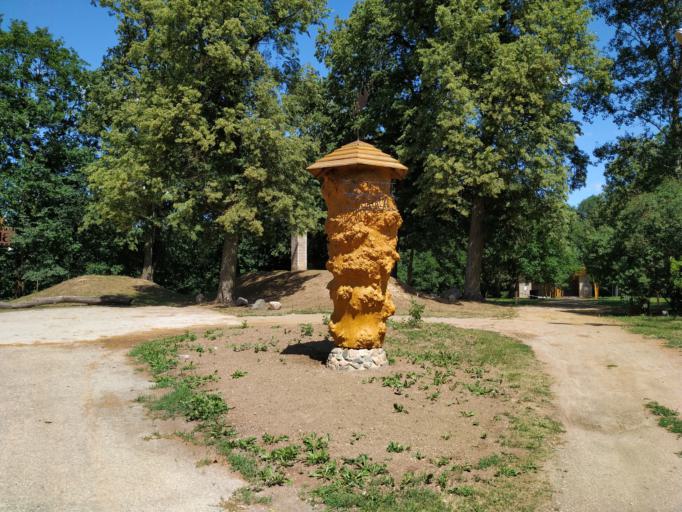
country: LT
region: Panevezys
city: Pasvalys
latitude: 56.2302
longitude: 24.4168
